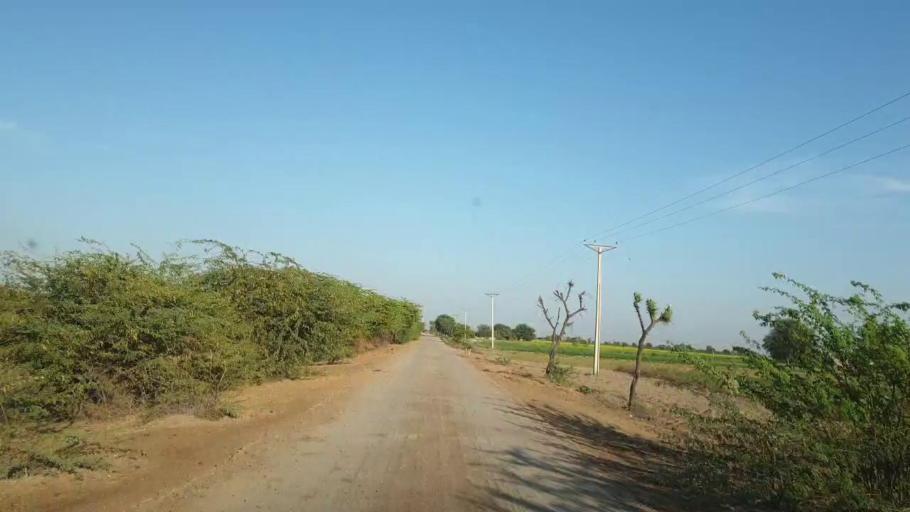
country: PK
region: Sindh
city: Kunri
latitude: 25.0910
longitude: 69.4394
